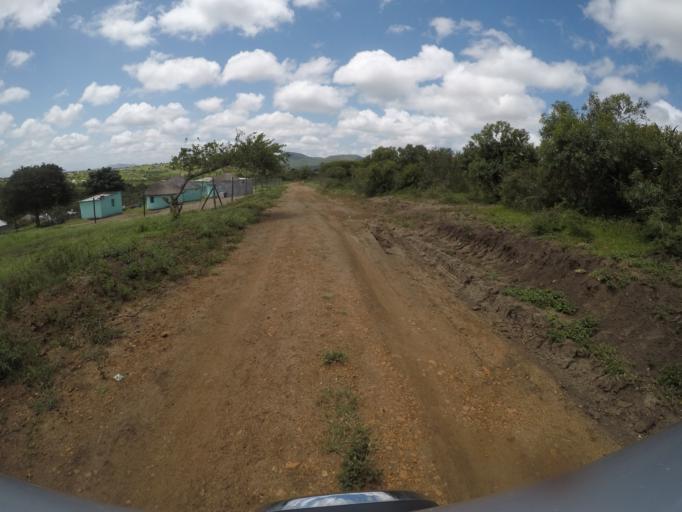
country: ZA
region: KwaZulu-Natal
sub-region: uThungulu District Municipality
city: Empangeni
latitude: -28.5838
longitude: 31.8315
